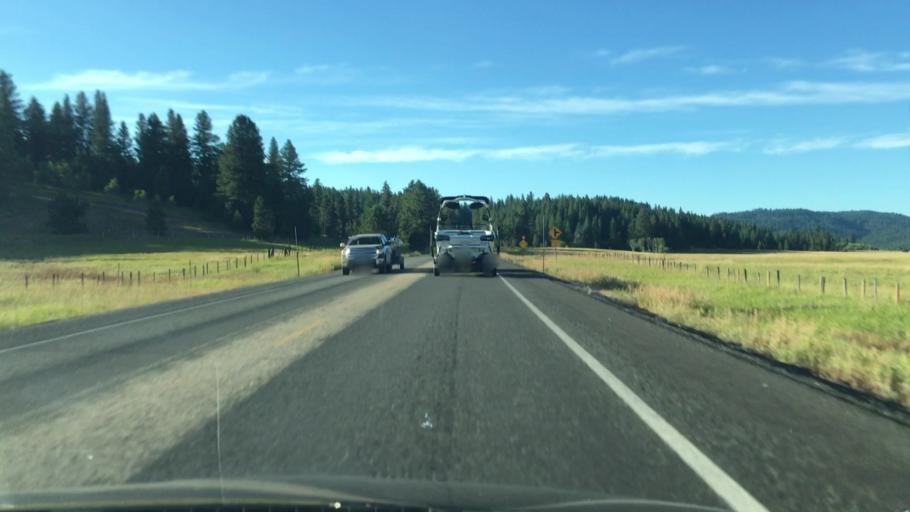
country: US
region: Idaho
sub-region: Valley County
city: Cascade
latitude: 44.5541
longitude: -116.0280
